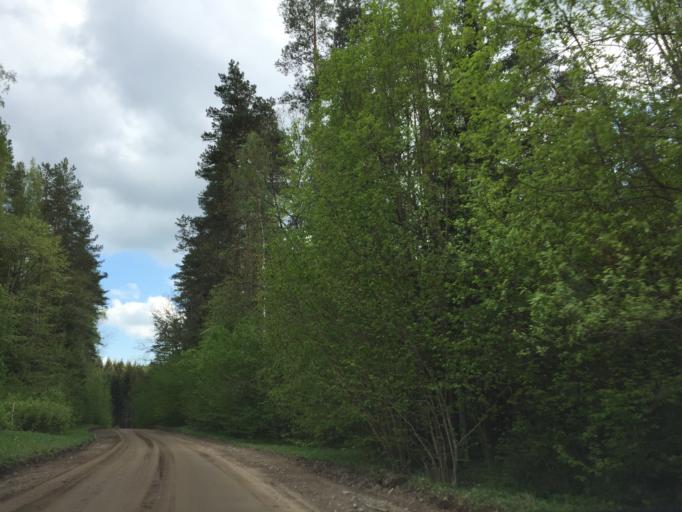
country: LV
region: Sigulda
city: Sigulda
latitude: 57.3108
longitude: 24.8825
